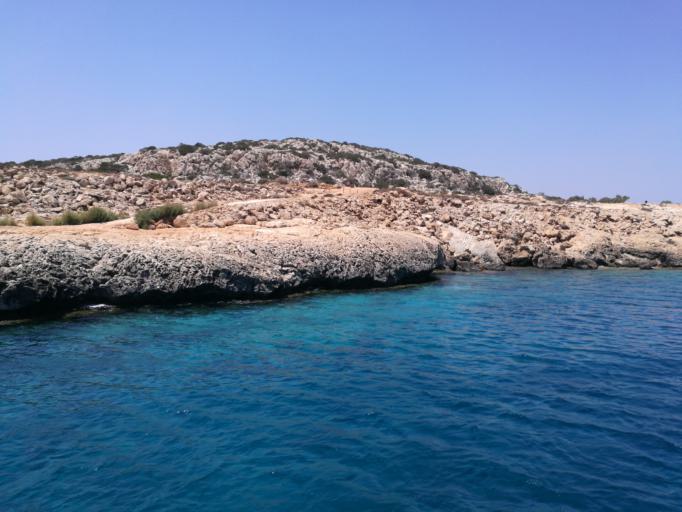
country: CY
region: Ammochostos
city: Protaras
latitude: 34.9725
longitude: 34.0770
